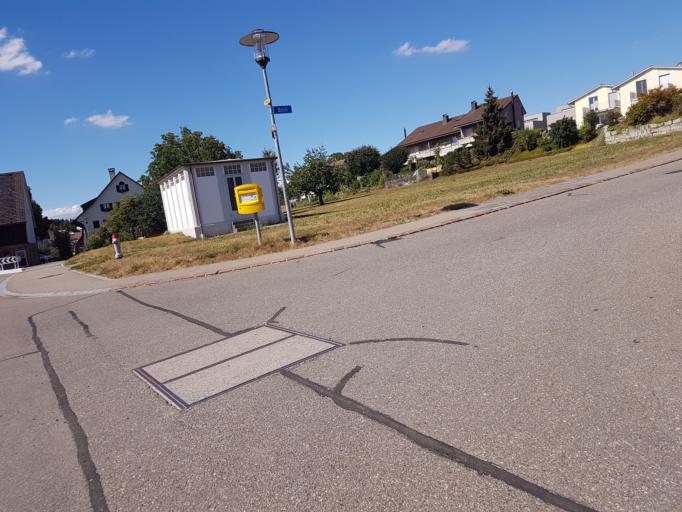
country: CH
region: Zurich
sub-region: Bezirk Pfaeffikon
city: Tagelswangen
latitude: 47.4281
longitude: 8.6735
